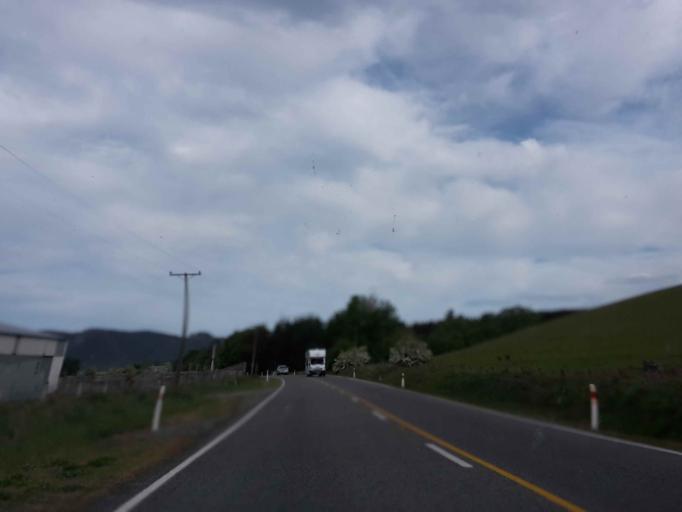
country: NZ
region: Canterbury
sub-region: Timaru District
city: Pleasant Point
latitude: -44.1077
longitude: 171.0088
